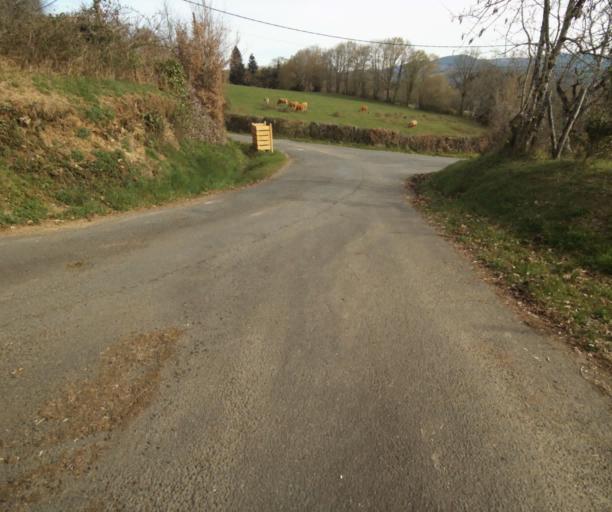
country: FR
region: Limousin
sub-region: Departement de la Correze
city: Seilhac
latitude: 45.4121
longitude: 1.7865
